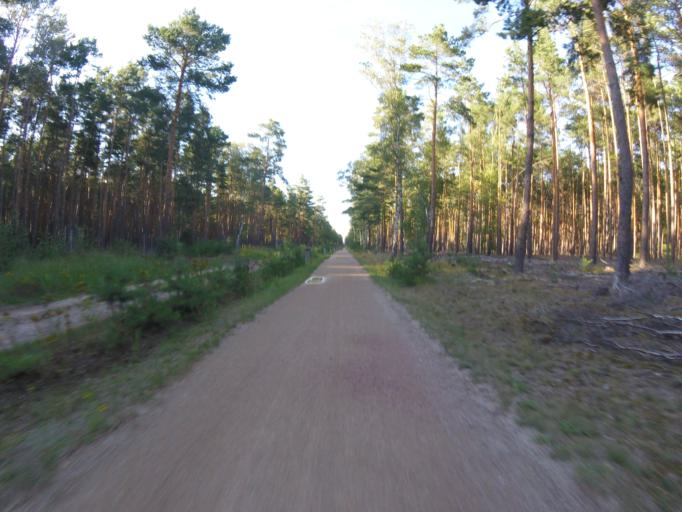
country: DE
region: Brandenburg
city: Halbe
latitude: 52.1864
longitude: 13.7591
